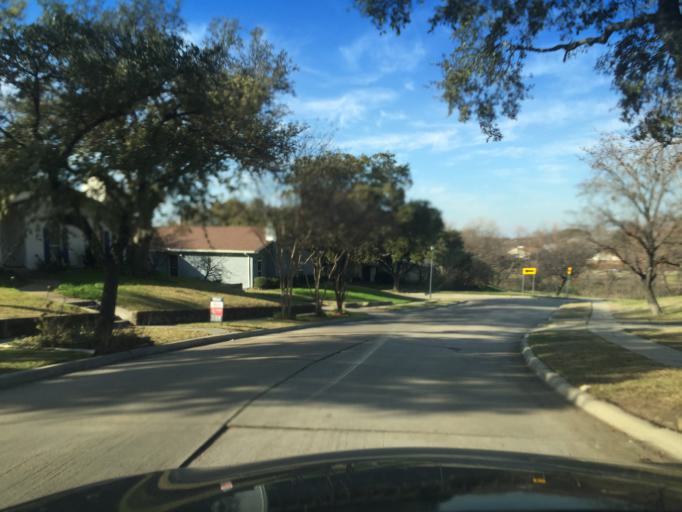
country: US
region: Texas
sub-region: Dallas County
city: Carrollton
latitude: 32.9949
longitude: -96.8911
